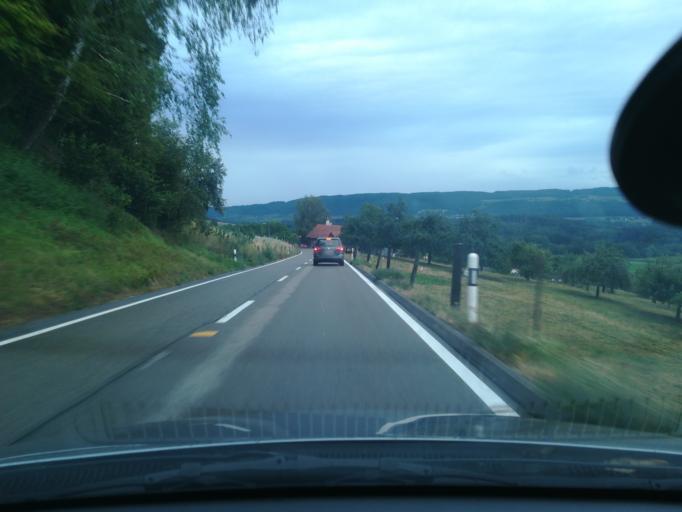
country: CH
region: Thurgau
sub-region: Frauenfeld District
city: Huttwilen
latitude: 47.6059
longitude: 8.9015
